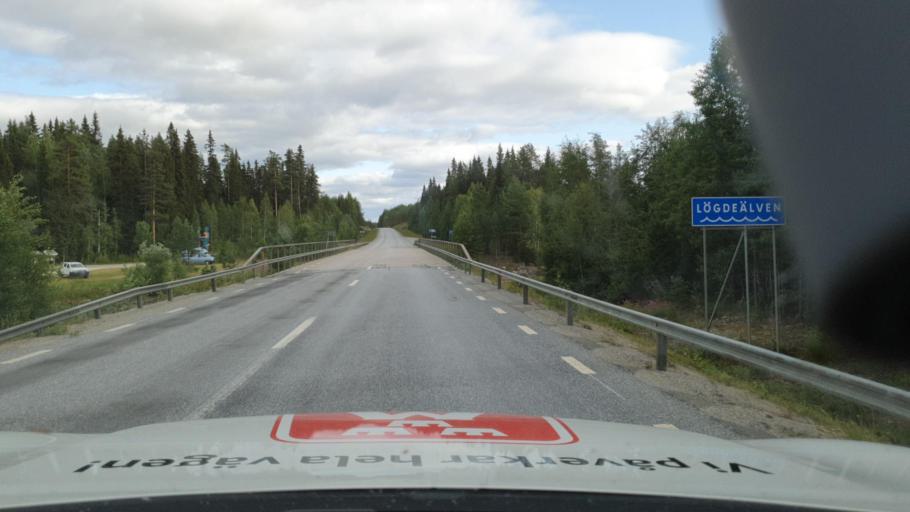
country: SE
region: Vaesterbotten
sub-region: Bjurholms Kommun
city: Bjurholm
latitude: 63.9917
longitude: 18.7967
